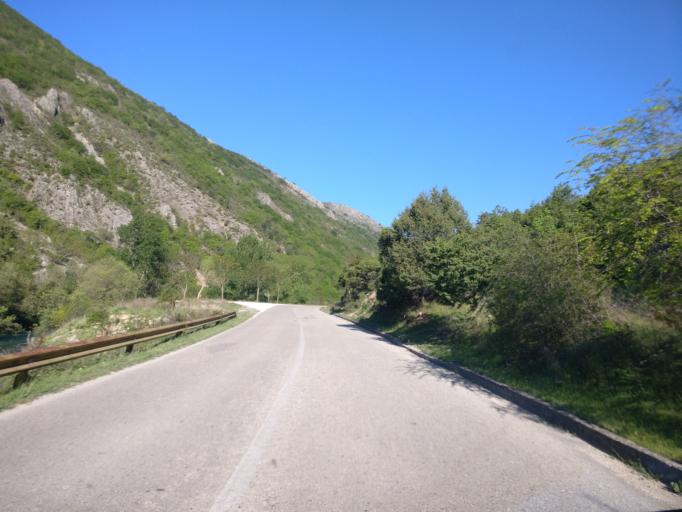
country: BA
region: Federation of Bosnia and Herzegovina
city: Stolac
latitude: 43.0846
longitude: 18.0067
